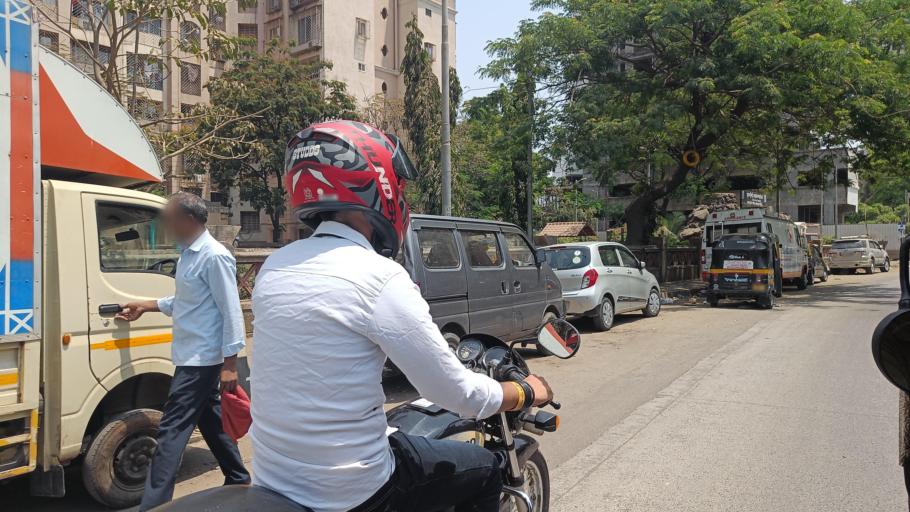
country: IN
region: Maharashtra
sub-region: Mumbai Suburban
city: Powai
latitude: 19.1379
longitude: 72.8410
